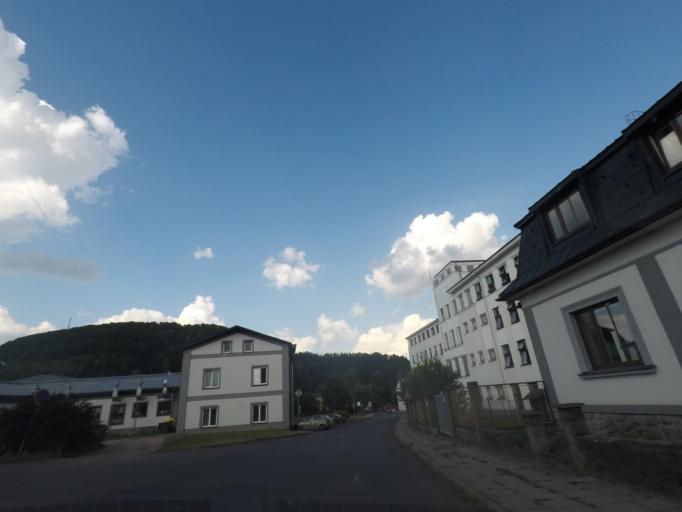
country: CZ
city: Radvanice
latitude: 50.6236
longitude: 16.0797
